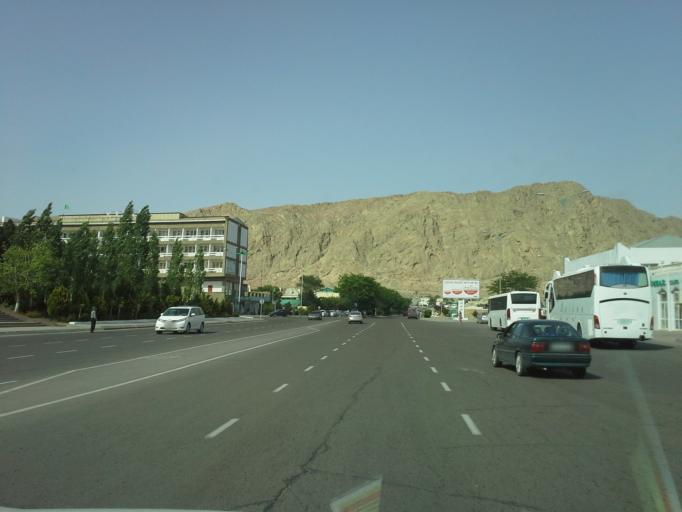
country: TM
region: Balkan
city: Turkmenbasy
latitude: 40.0039
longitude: 52.9946
